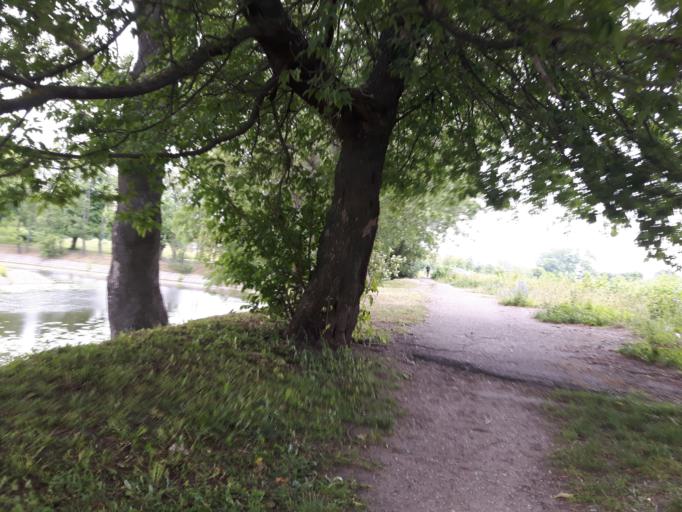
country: LT
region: Klaipedos apskritis
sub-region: Klaipeda
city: Klaipeda
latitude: 55.7094
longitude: 21.1408
